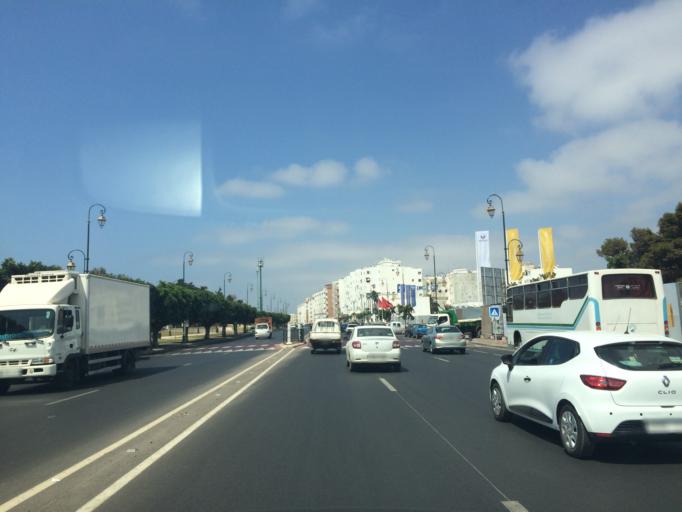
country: MA
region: Rabat-Sale-Zemmour-Zaer
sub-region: Rabat
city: Rabat
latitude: 33.9940
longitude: -6.8640
